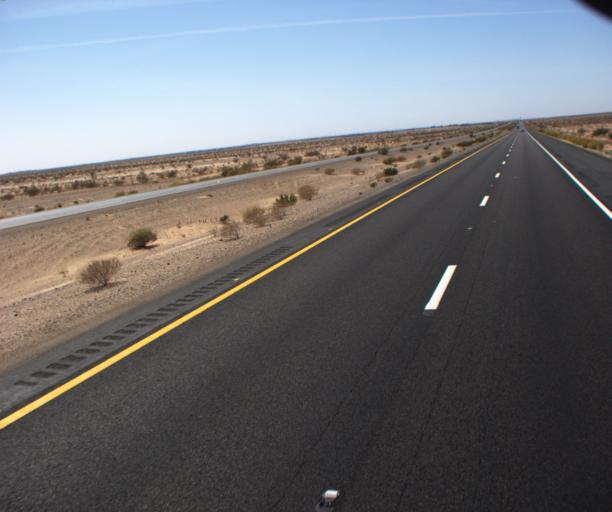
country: US
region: Arizona
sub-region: Yuma County
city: Somerton
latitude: 32.4954
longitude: -114.6116
